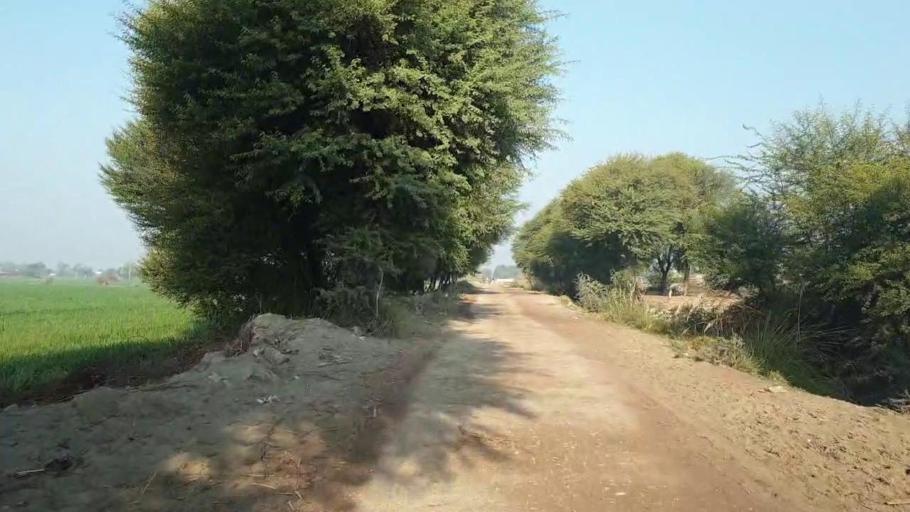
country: PK
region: Sindh
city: Shahdadpur
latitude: 25.9701
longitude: 68.6147
